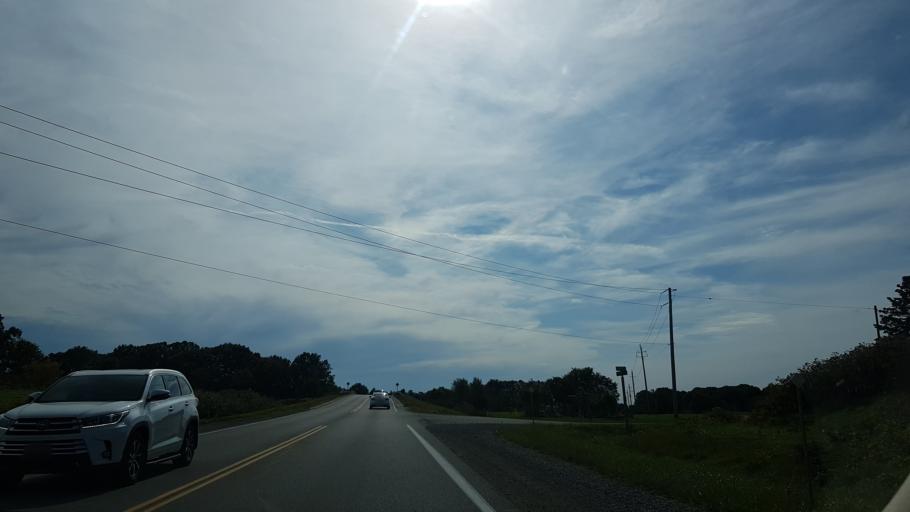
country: CA
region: Ontario
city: Delaware
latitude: 42.9739
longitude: -81.3920
